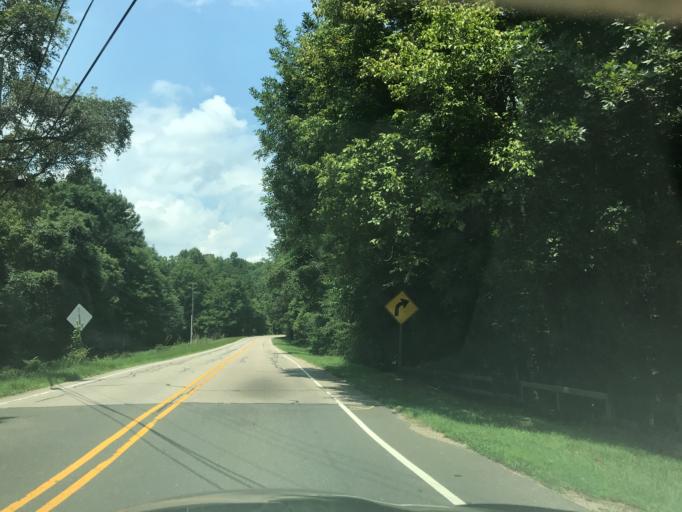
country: US
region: North Carolina
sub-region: Wake County
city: West Raleigh
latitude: 35.8342
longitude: -78.7201
